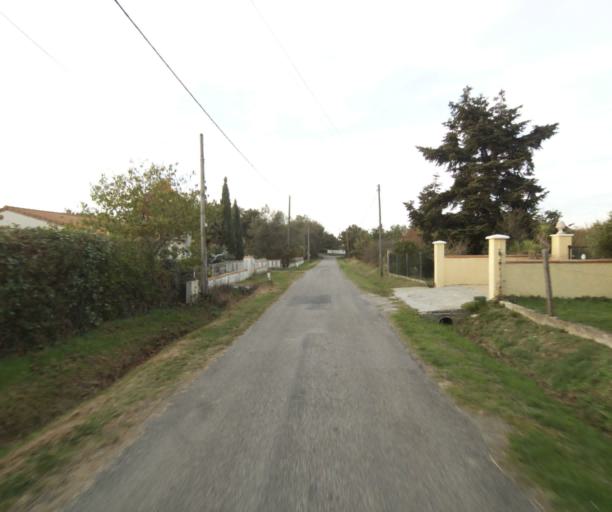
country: FR
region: Midi-Pyrenees
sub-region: Departement du Tarn-et-Garonne
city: Pompignan
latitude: 43.8250
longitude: 1.3142
